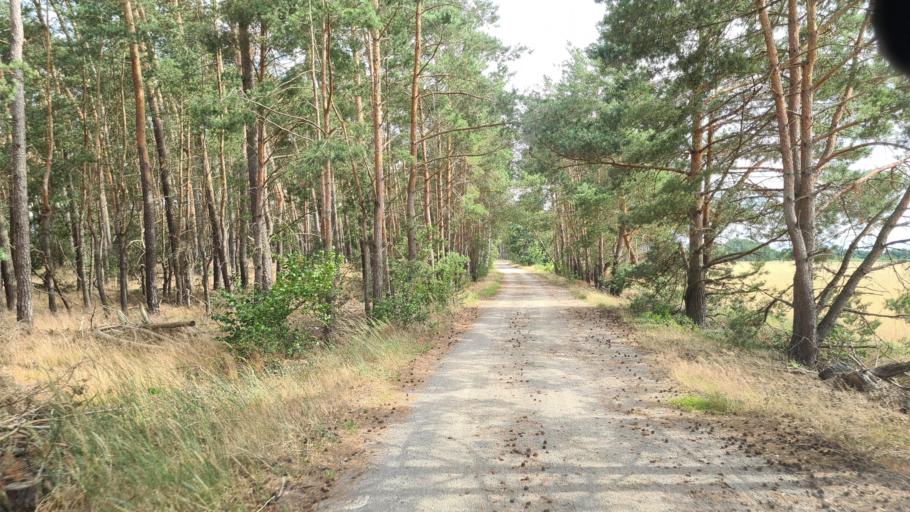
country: DE
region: Saxony-Anhalt
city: Holzdorf
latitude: 51.8137
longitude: 13.2039
